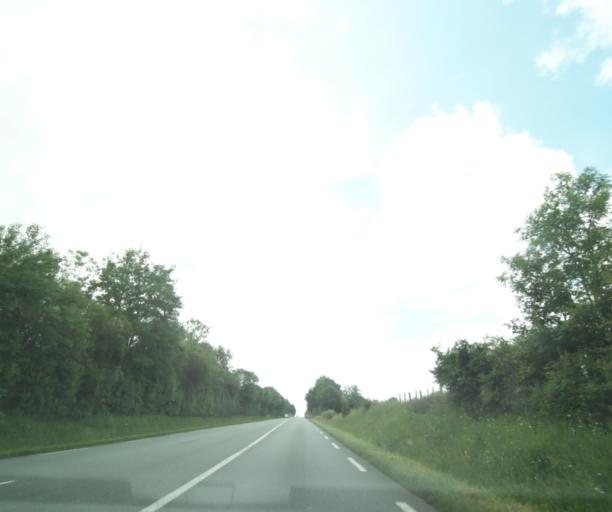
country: FR
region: Poitou-Charentes
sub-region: Departement des Deux-Sevres
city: Saint-Pardoux
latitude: 46.5582
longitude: -0.3056
